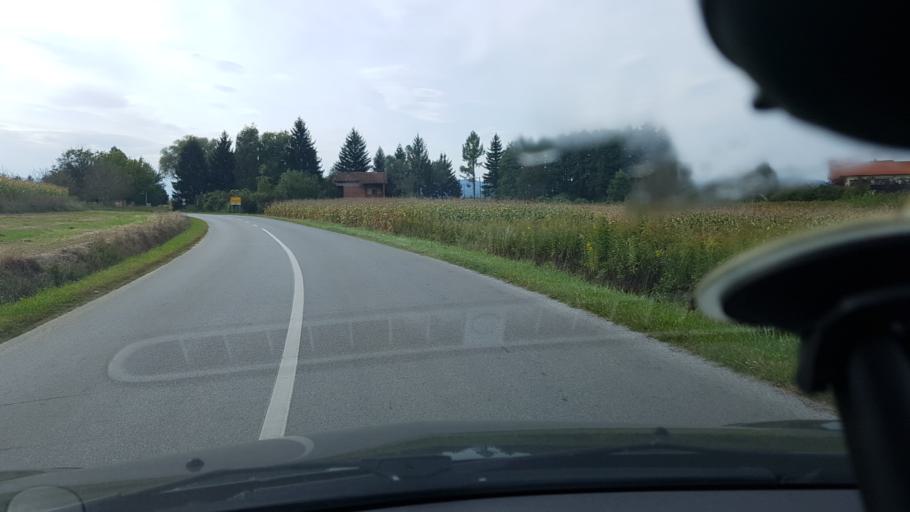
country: HR
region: Varazdinska
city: Ivanec
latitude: 46.2353
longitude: 16.1577
